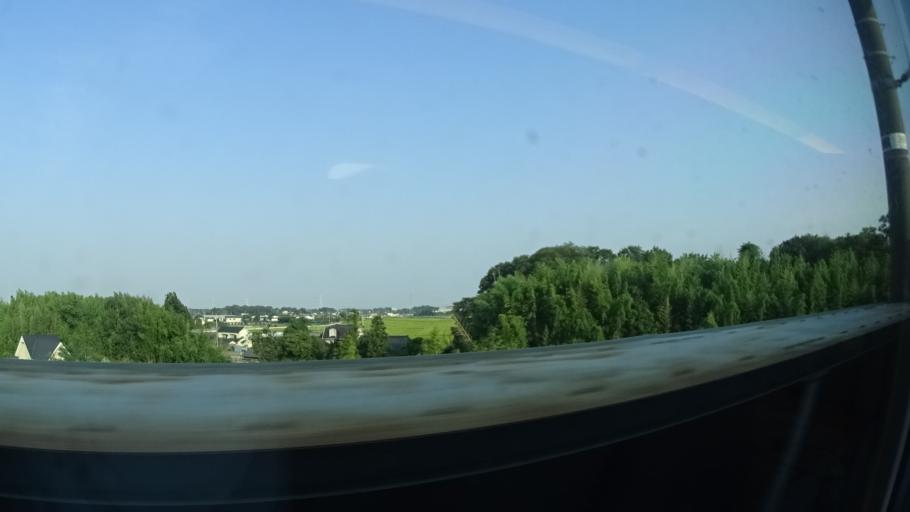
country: JP
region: Saitama
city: Kurihashi
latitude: 36.1296
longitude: 139.7174
